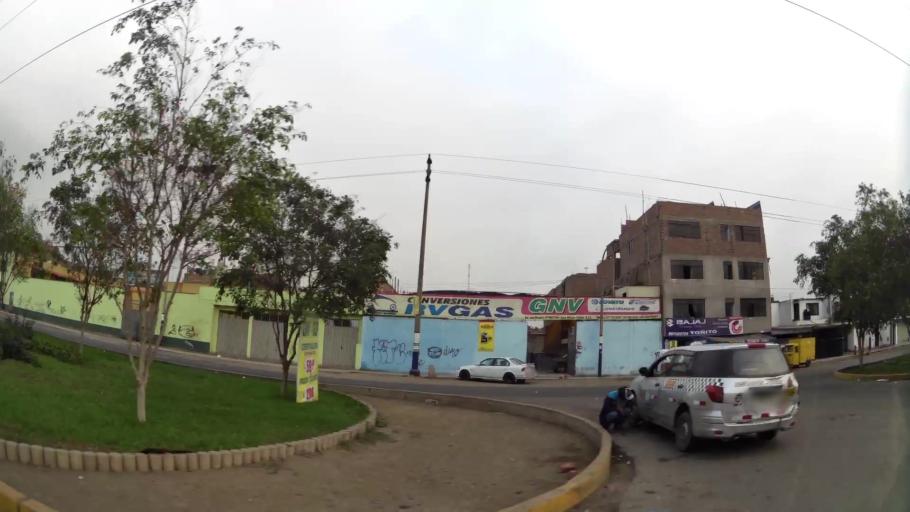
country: PE
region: Lima
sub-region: Lima
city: Independencia
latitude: -11.9961
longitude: -77.0038
